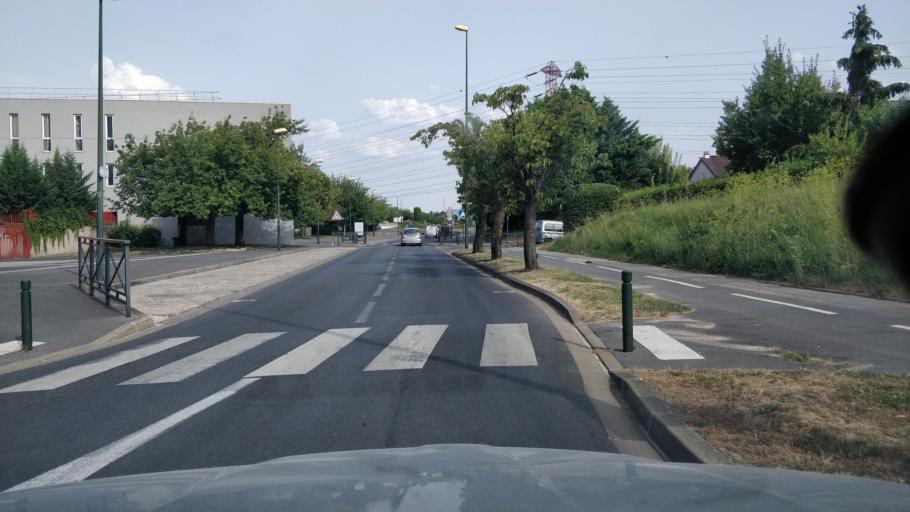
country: FR
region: Ile-de-France
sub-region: Departement de Seine-et-Marne
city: Chelles
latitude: 48.8887
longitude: 2.6117
